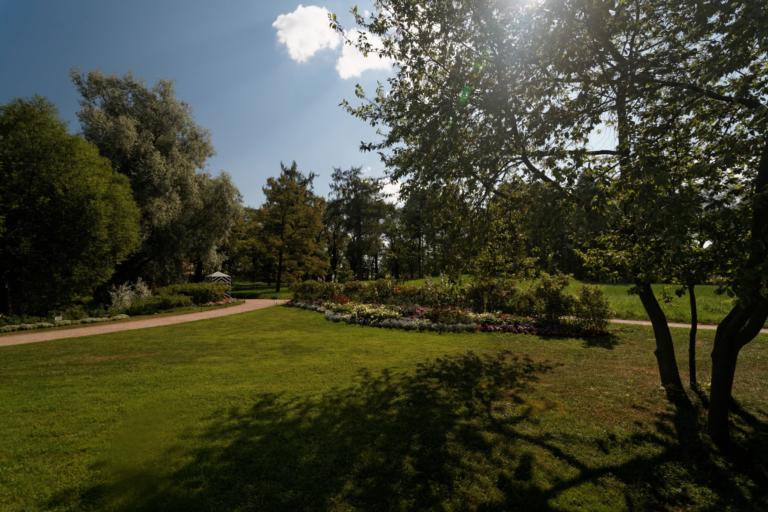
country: RU
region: St.-Petersburg
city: Pushkin
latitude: 59.7094
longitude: 30.3903
